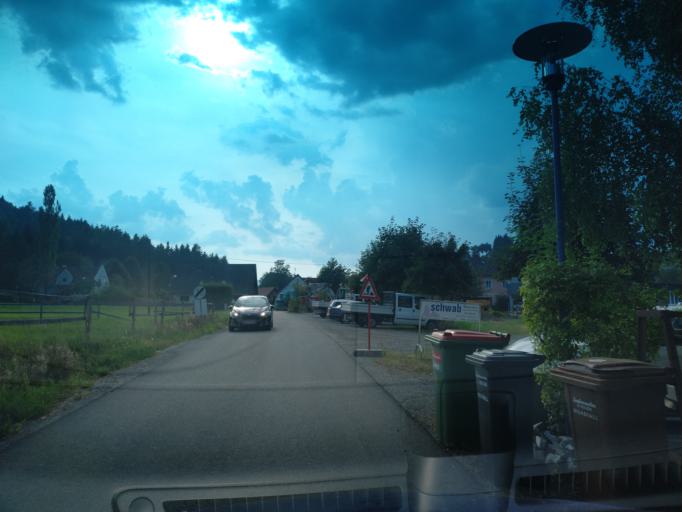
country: AT
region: Styria
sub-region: Politischer Bezirk Deutschlandsberg
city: Wies
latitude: 46.7180
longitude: 15.2745
